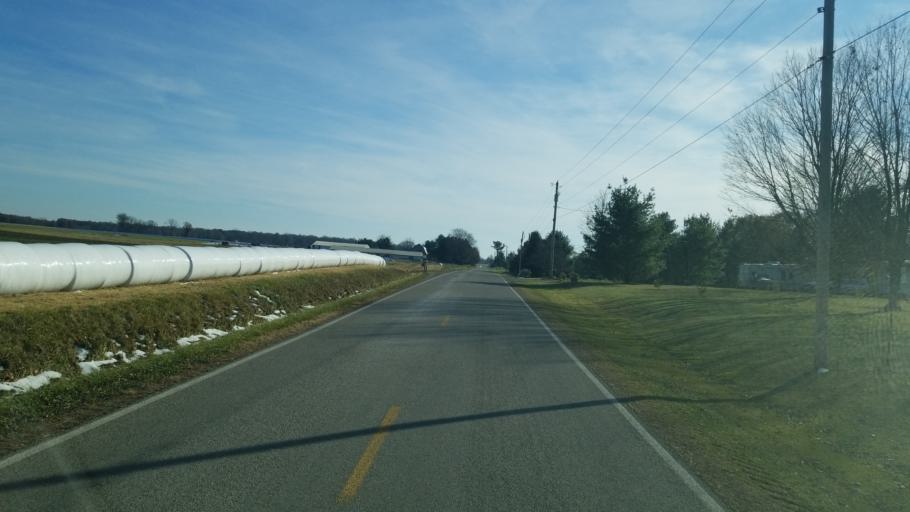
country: US
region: Ohio
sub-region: Lorain County
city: Camden
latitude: 41.1934
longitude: -82.3584
